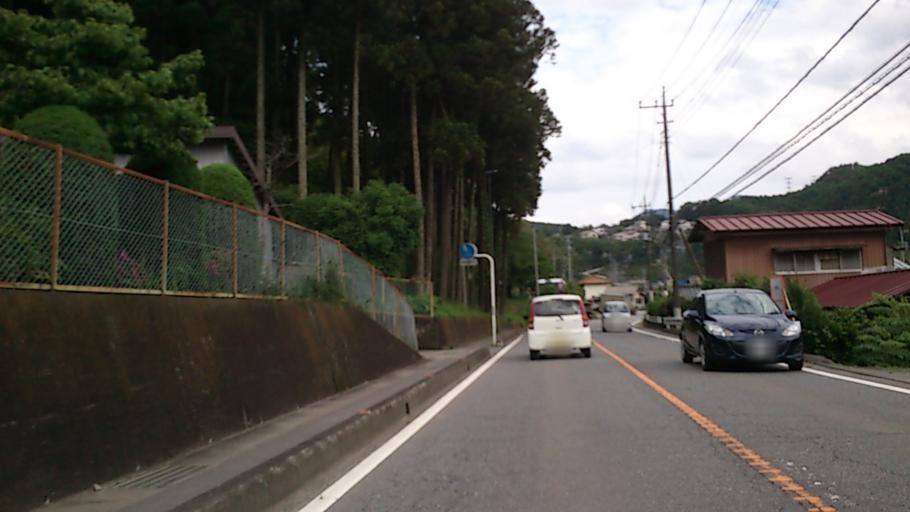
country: JP
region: Gunma
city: Tomioka
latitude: 36.2186
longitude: 138.8011
